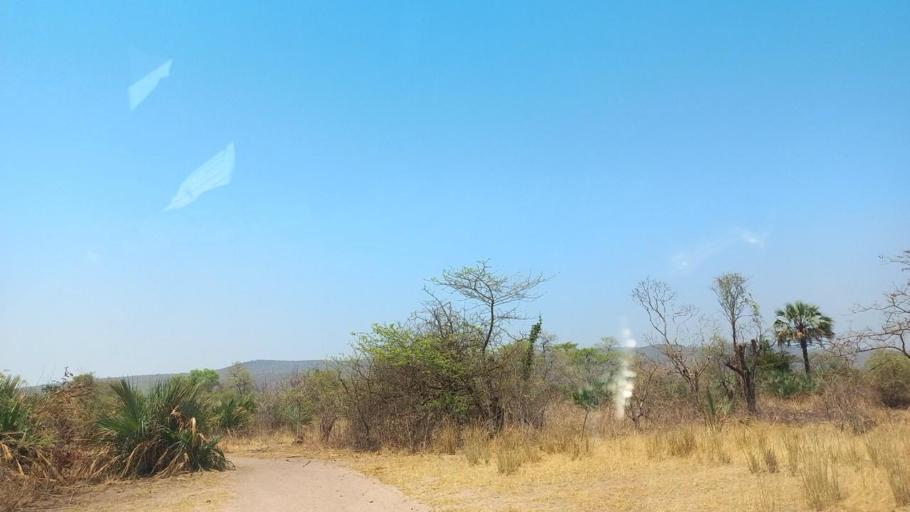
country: ZM
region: Lusaka
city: Luangwa
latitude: -15.1998
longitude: 30.1902
